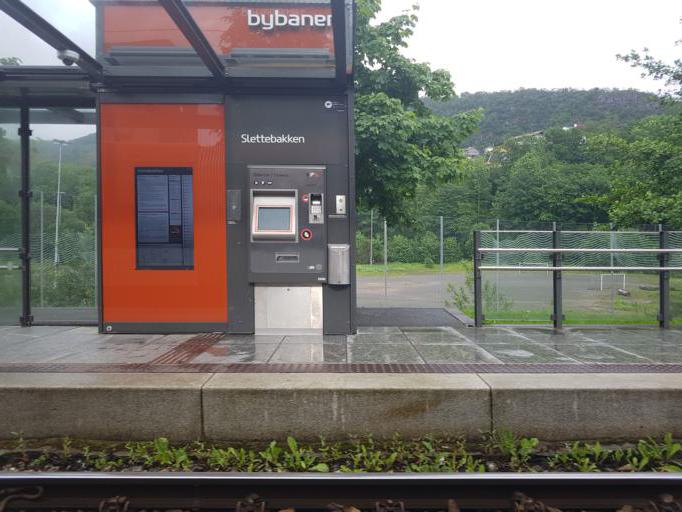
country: NO
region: Hordaland
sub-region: Bergen
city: Bergen
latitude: 60.3504
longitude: 5.3598
